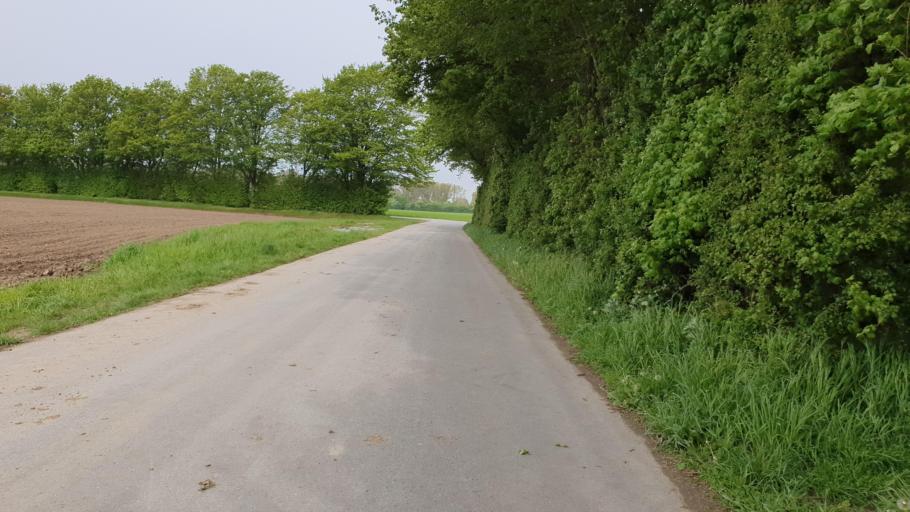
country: DE
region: North Rhine-Westphalia
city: Monheim am Rhein
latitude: 51.0815
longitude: 6.8736
